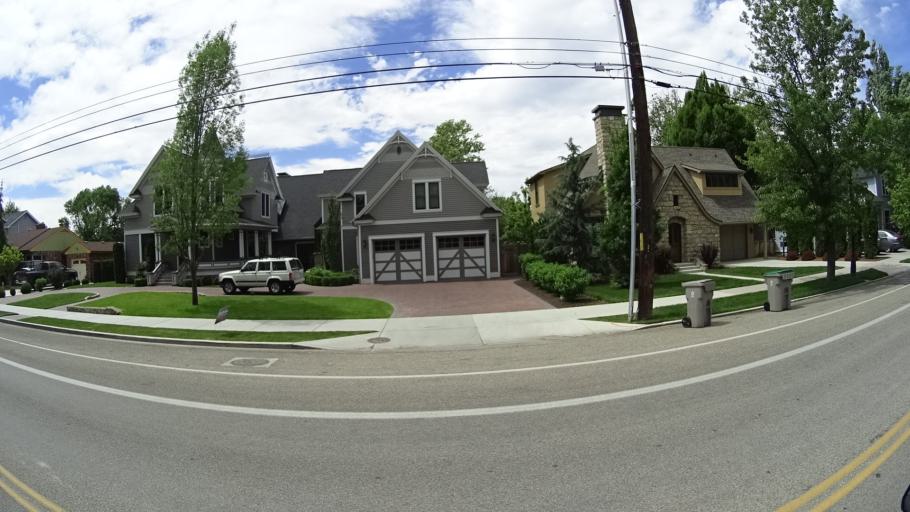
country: US
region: Idaho
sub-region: Ada County
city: Boise
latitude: 43.6051
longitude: -116.1781
